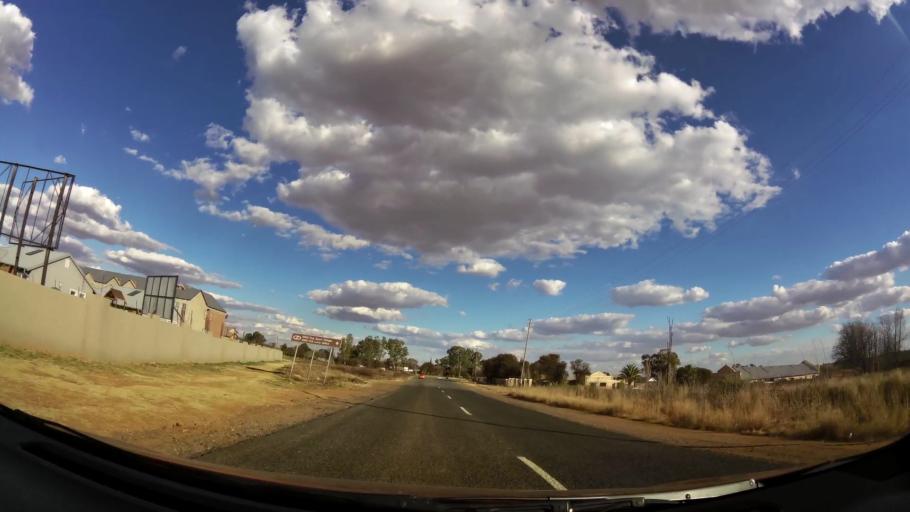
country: ZA
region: North-West
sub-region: Dr Kenneth Kaunda District Municipality
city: Potchefstroom
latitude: -26.6701
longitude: 27.1059
